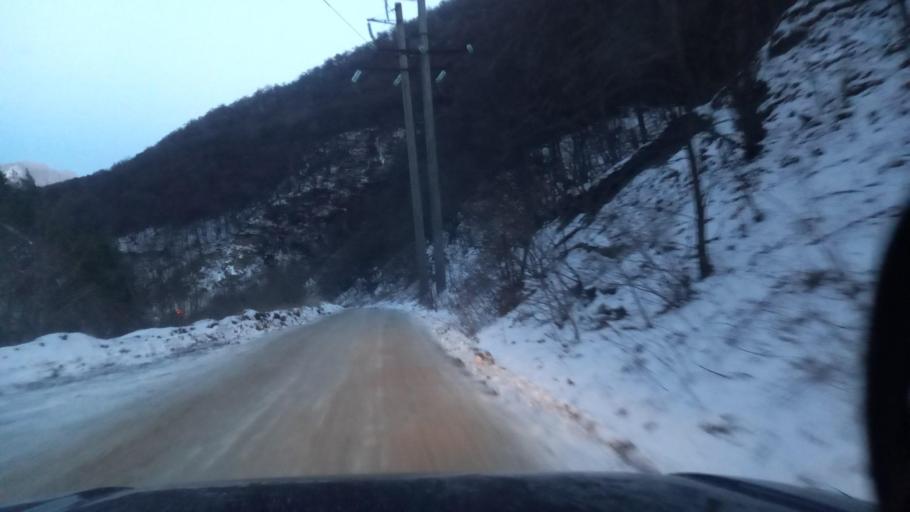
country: RU
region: Ingushetiya
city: Dzhayrakh
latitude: 42.8248
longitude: 44.5962
